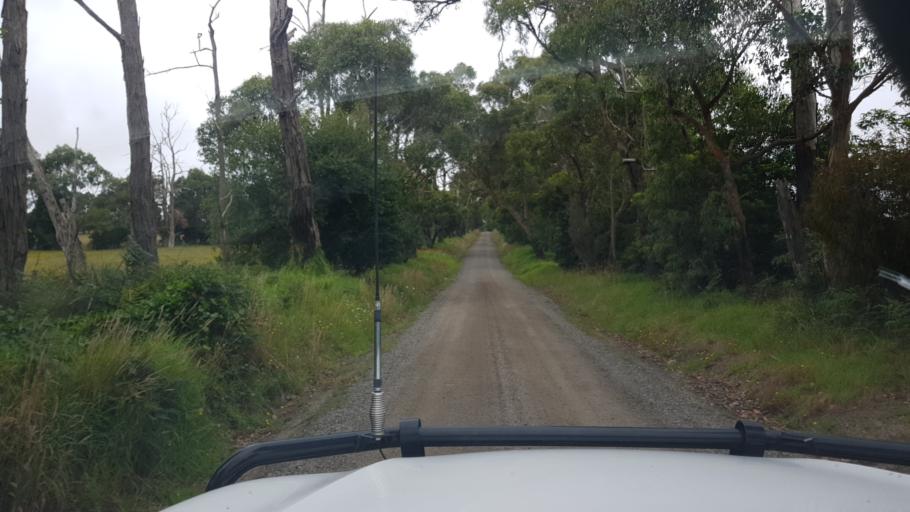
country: AU
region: Victoria
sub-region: Baw Baw
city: Warragul
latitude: -38.1856
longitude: 145.8316
